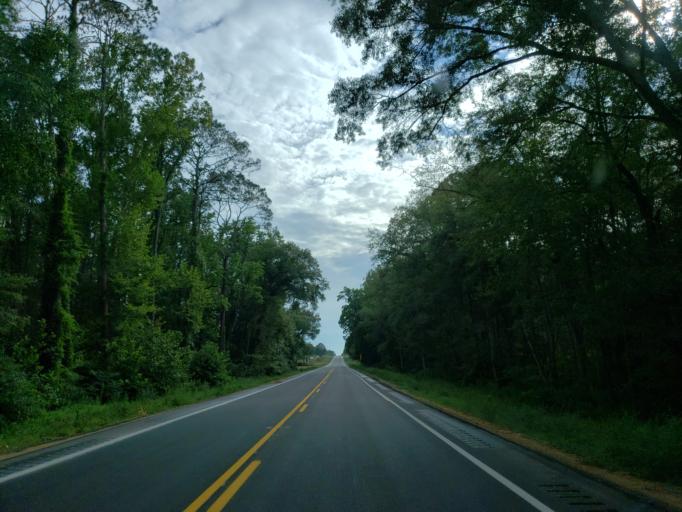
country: US
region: Georgia
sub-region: Irwin County
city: Ocilla
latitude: 31.5936
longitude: -83.2624
